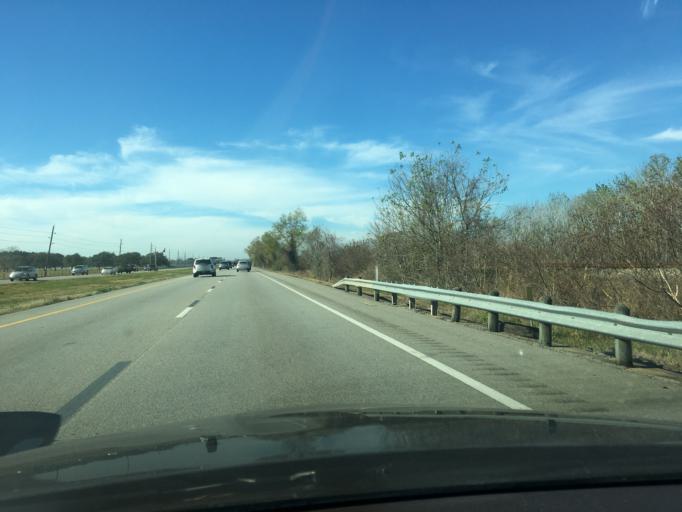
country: US
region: Texas
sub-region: Fort Bend County
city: Pecan Grove
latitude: 29.5986
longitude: -95.7163
